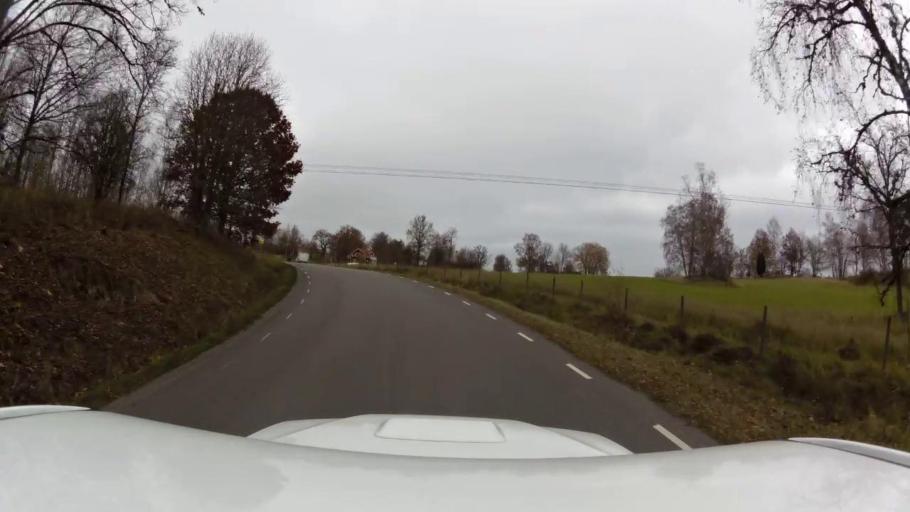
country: SE
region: OEstergoetland
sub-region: Kinda Kommun
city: Rimforsa
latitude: 58.2260
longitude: 15.6858
